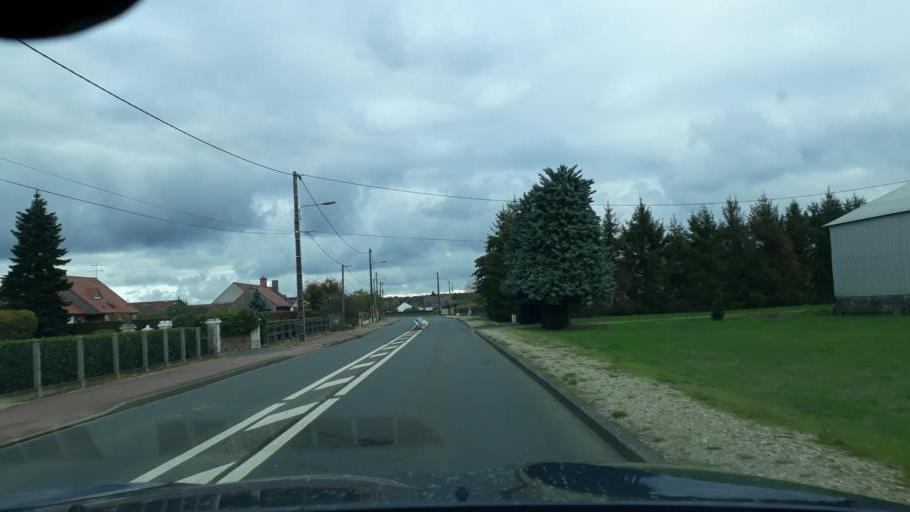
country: FR
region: Centre
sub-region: Departement du Loiret
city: Bray-en-Val
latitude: 47.7995
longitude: 2.3887
